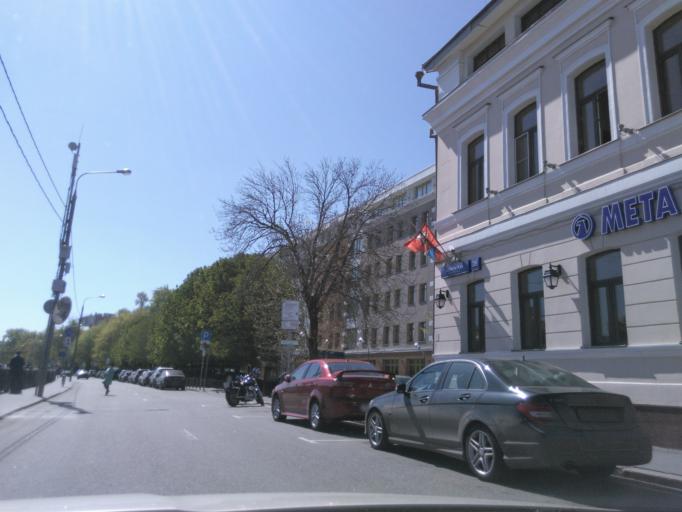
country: RU
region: Moscow
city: Zamoskvorech'ye
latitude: 55.7389
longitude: 37.6386
